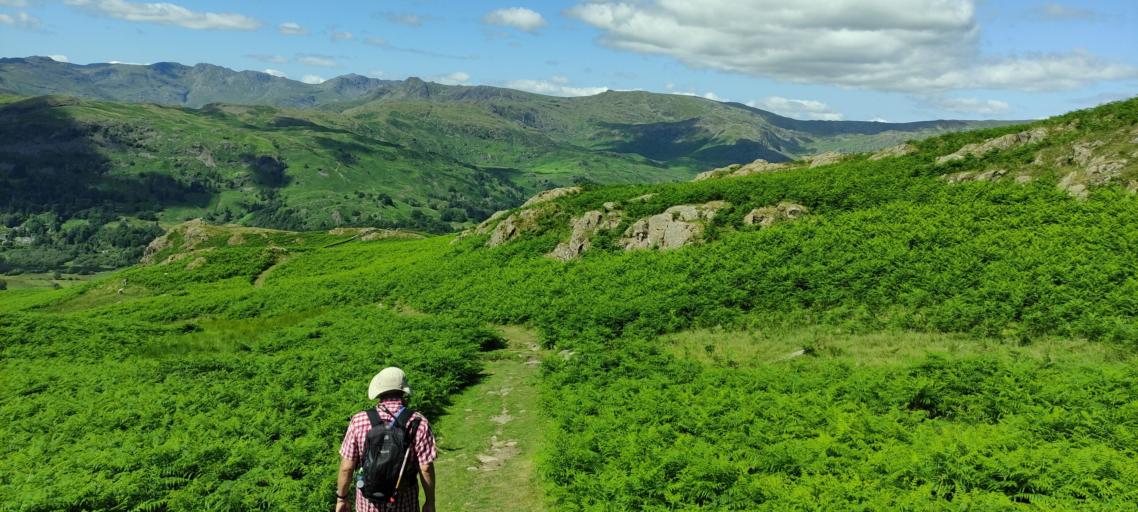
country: GB
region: England
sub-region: Cumbria
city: Ambleside
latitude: 54.4610
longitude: -3.0022
